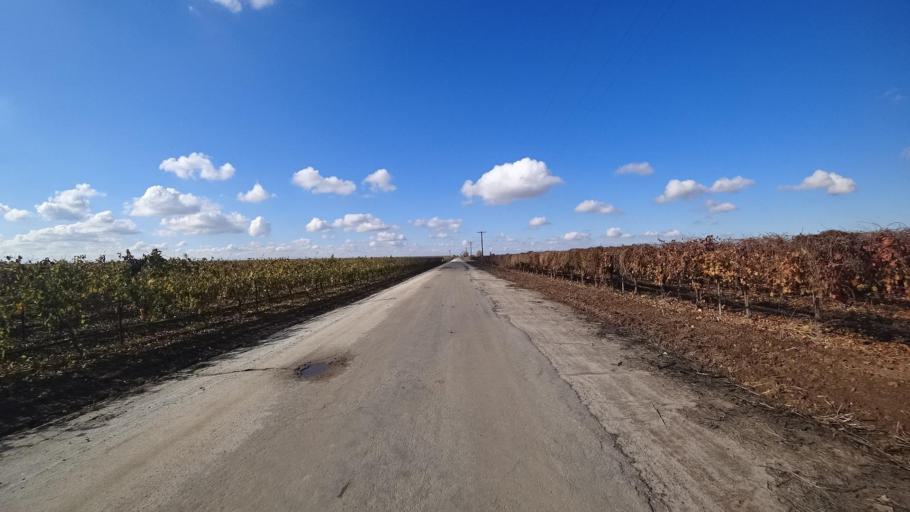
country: US
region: California
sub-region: Kern County
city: McFarland
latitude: 35.6600
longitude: -119.2092
